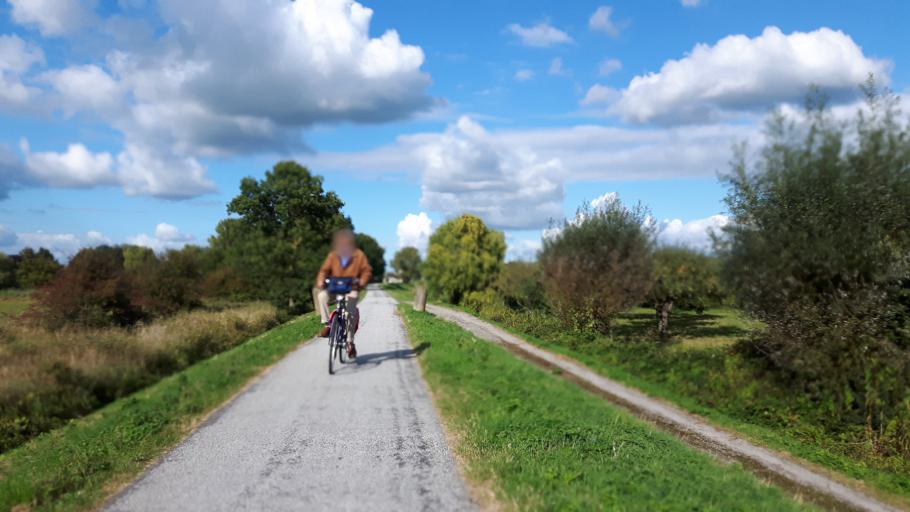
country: NL
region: South Holland
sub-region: Gemeente Leerdam
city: Leerdam
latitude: 51.8811
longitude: 5.0890
